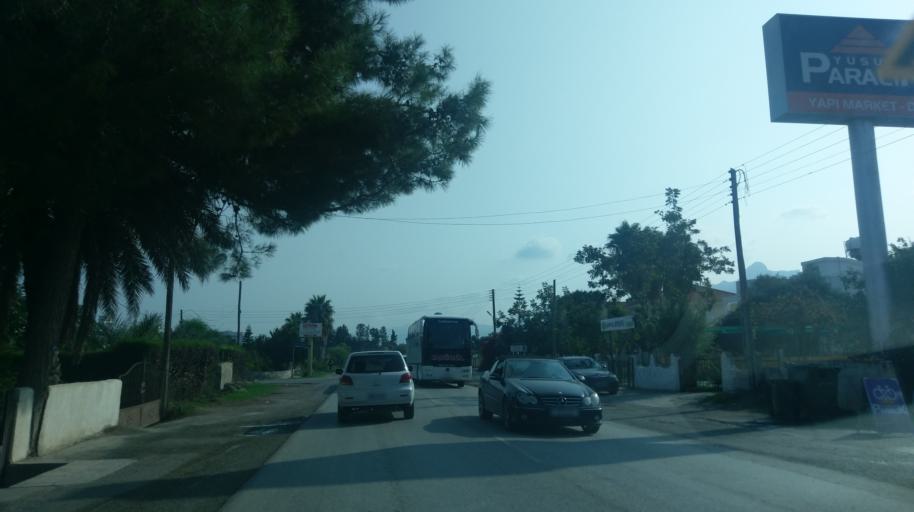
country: CY
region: Keryneia
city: Kyrenia
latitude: 35.3298
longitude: 33.3508
